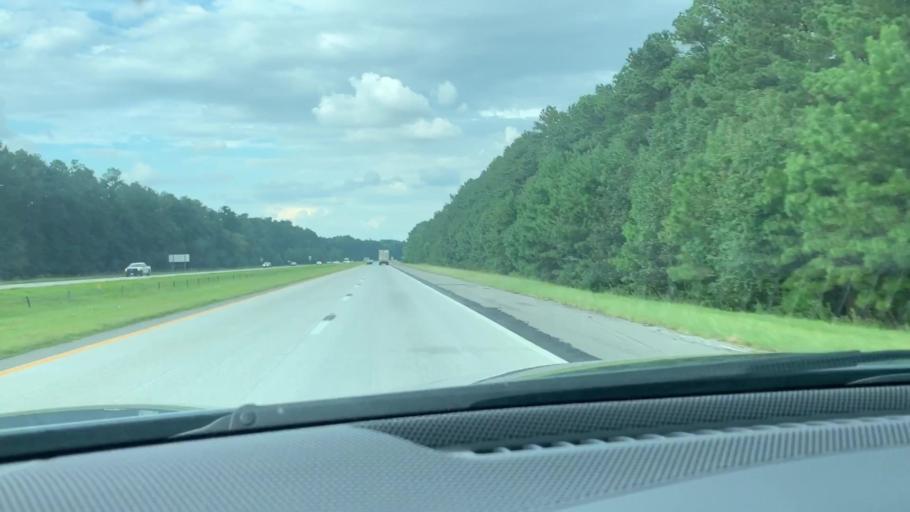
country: US
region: South Carolina
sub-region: Dorchester County
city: Saint George
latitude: 33.3029
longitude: -80.5553
